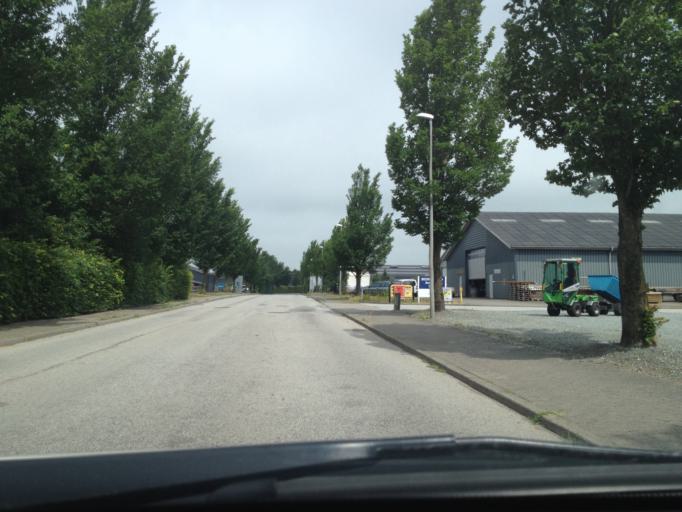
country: DK
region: South Denmark
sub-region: Esbjerg Kommune
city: Ribe
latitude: 55.3575
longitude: 8.7714
